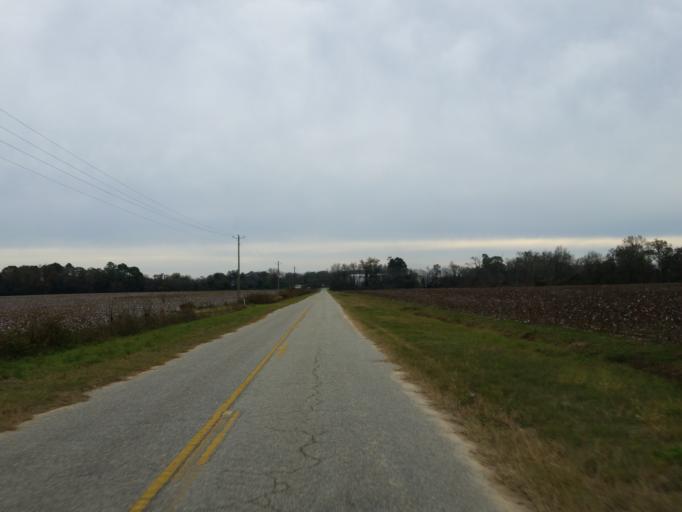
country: US
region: Georgia
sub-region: Dooly County
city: Vienna
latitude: 32.1613
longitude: -83.7754
